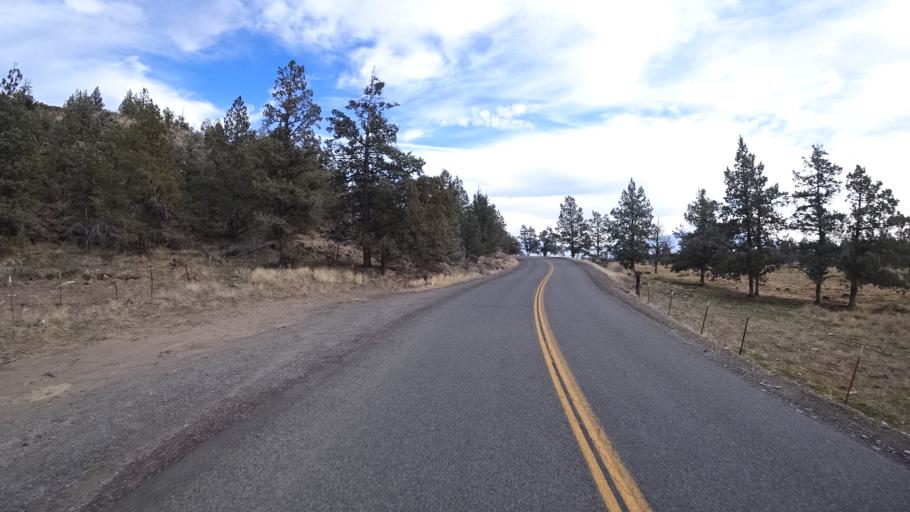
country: US
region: California
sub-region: Siskiyou County
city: Montague
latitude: 41.6384
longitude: -122.4350
